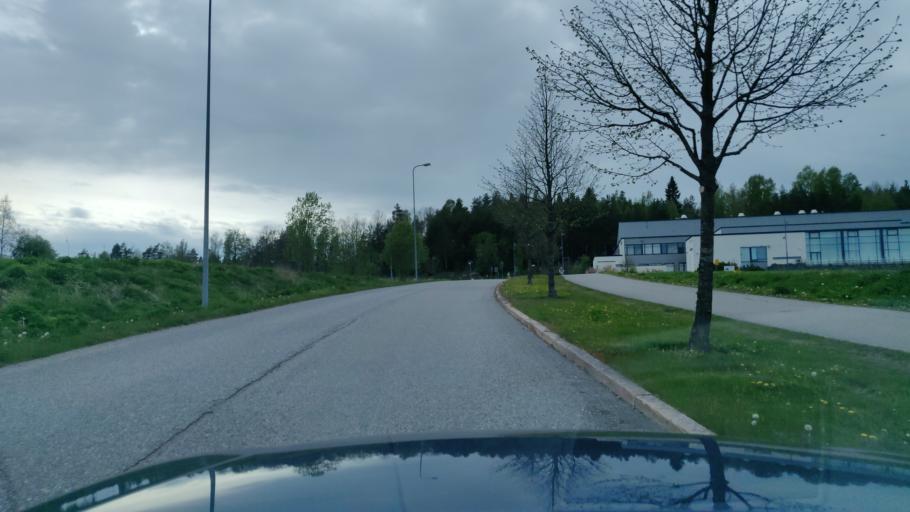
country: FI
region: Uusimaa
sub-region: Helsinki
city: Nurmijaervi
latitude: 60.3846
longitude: 24.7602
